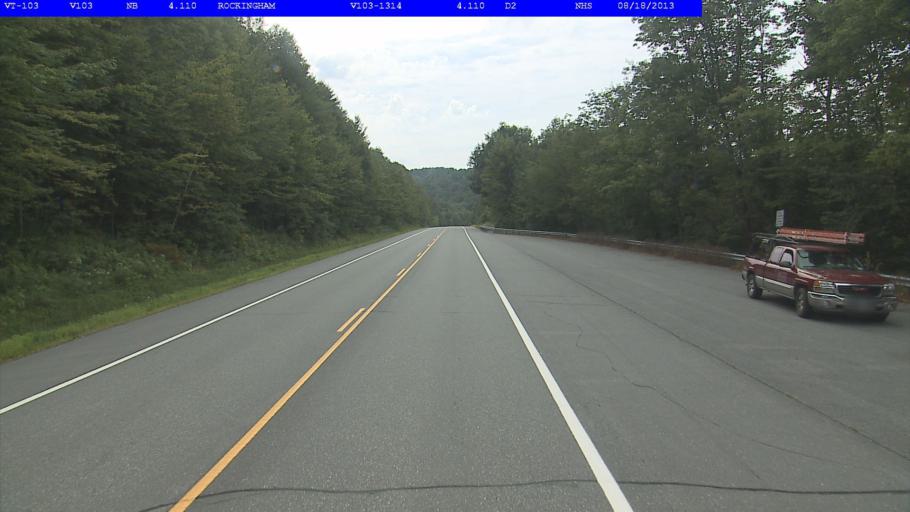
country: US
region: Vermont
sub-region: Windham County
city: Rockingham
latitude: 43.2052
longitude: -72.5291
